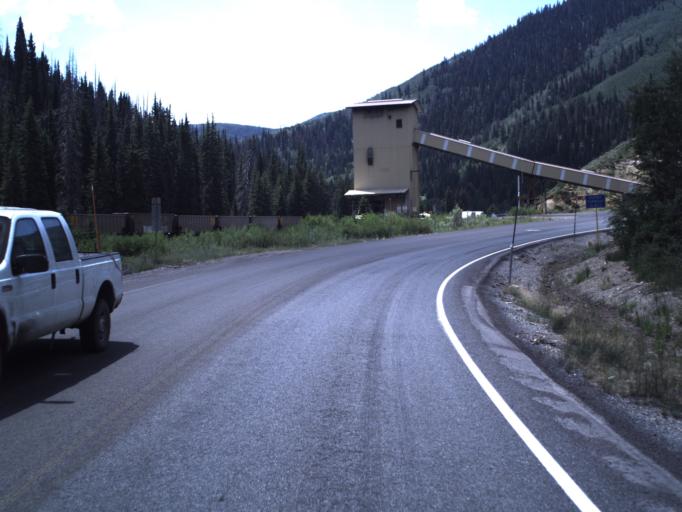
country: US
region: Utah
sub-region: Sanpete County
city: Fairview
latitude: 39.6859
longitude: -111.1548
